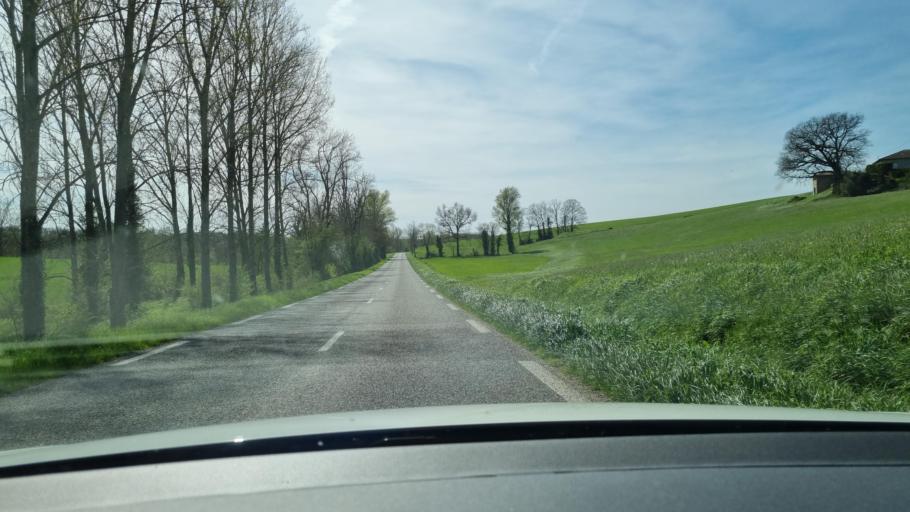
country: FR
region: Midi-Pyrenees
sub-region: Departement du Gers
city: Samatan
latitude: 43.4903
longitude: 0.9917
